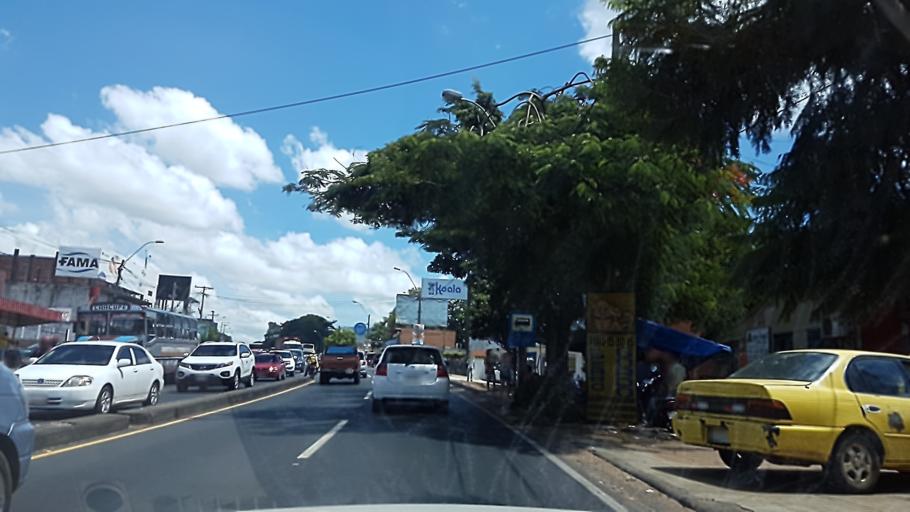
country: PY
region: Central
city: Capiata
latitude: -25.3527
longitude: -57.4439
